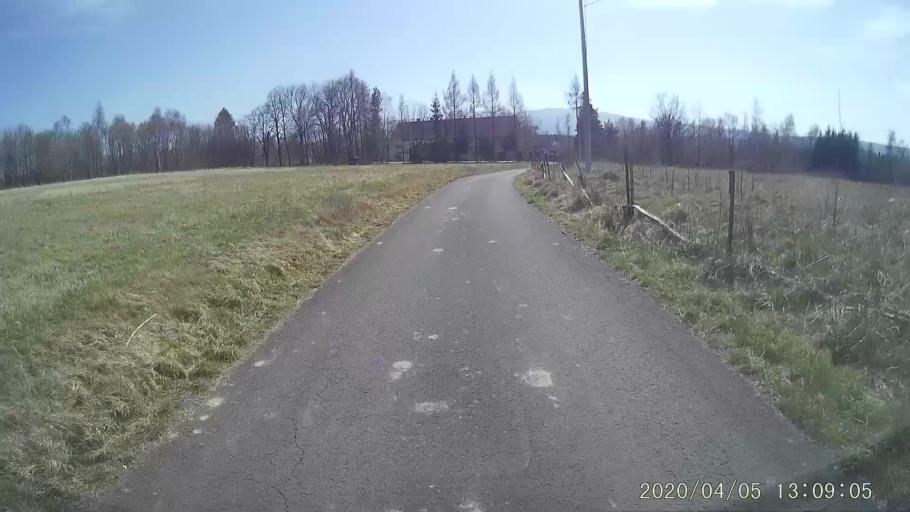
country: PL
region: Lower Silesian Voivodeship
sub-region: Powiat lubanski
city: Lesna
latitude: 50.9803
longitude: 15.3007
